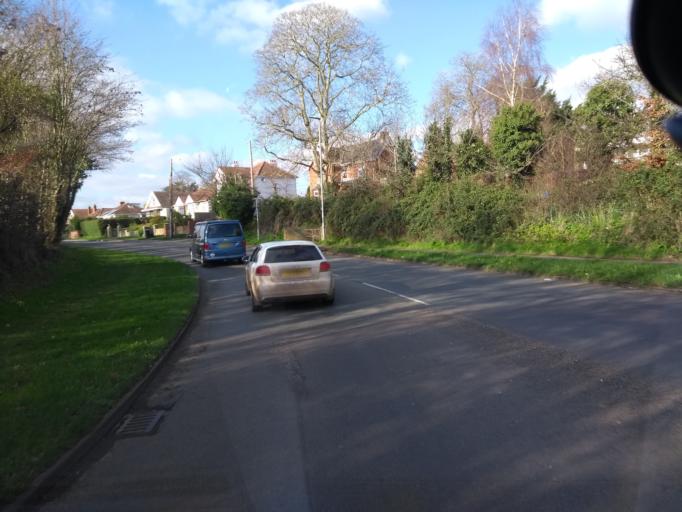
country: GB
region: England
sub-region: Somerset
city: Creech Saint Michael
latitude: 51.0178
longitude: -3.0697
